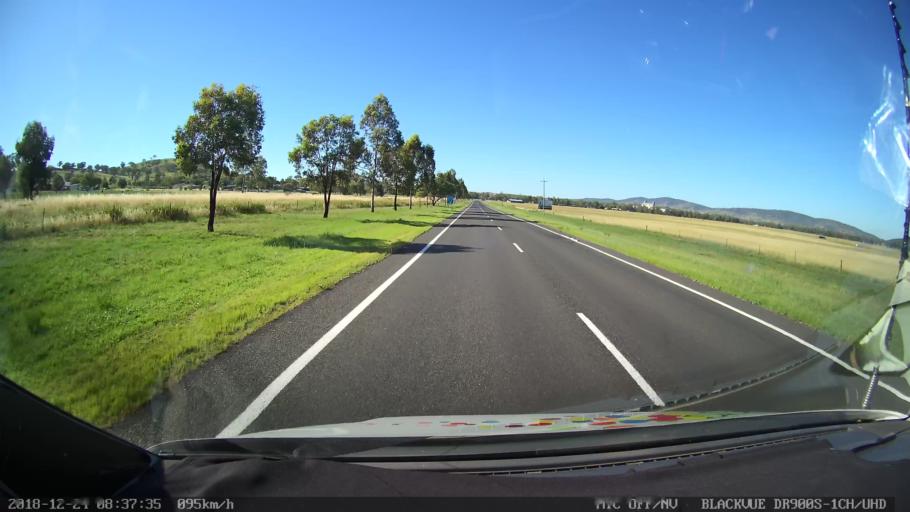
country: AU
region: New South Wales
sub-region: Liverpool Plains
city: Quirindi
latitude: -31.3310
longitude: 150.6485
